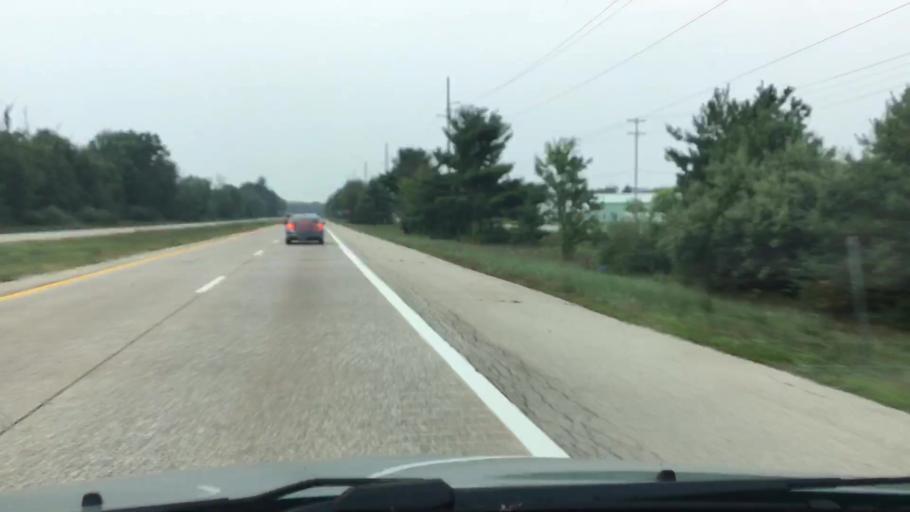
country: US
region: Michigan
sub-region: Ottawa County
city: Grand Haven
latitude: 43.0192
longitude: -86.2116
